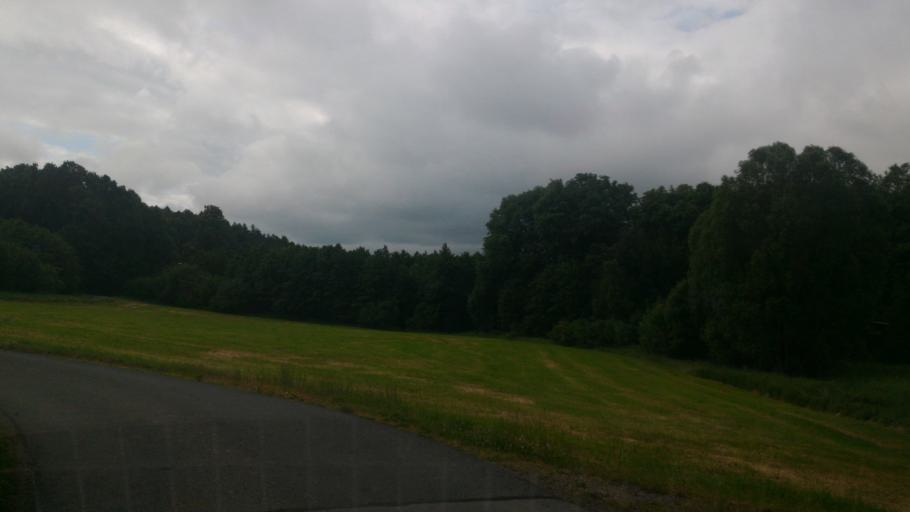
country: DE
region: Saxony
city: Neugersdorf
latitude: 50.9603
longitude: 14.6214
